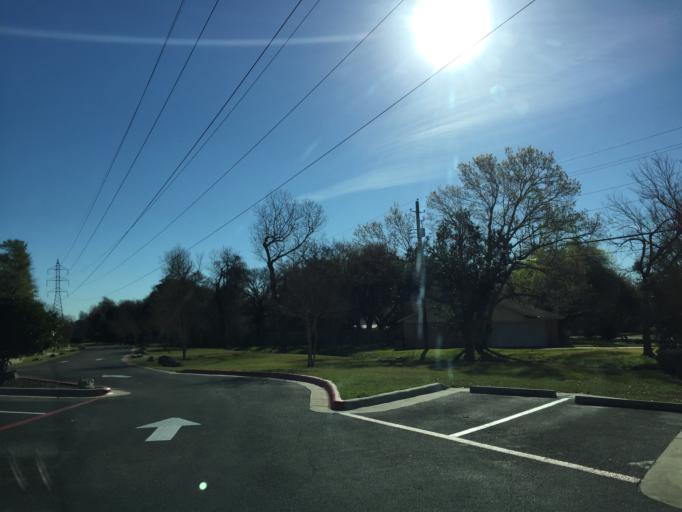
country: US
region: Texas
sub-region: Williamson County
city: Jollyville
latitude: 30.4046
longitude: -97.7382
